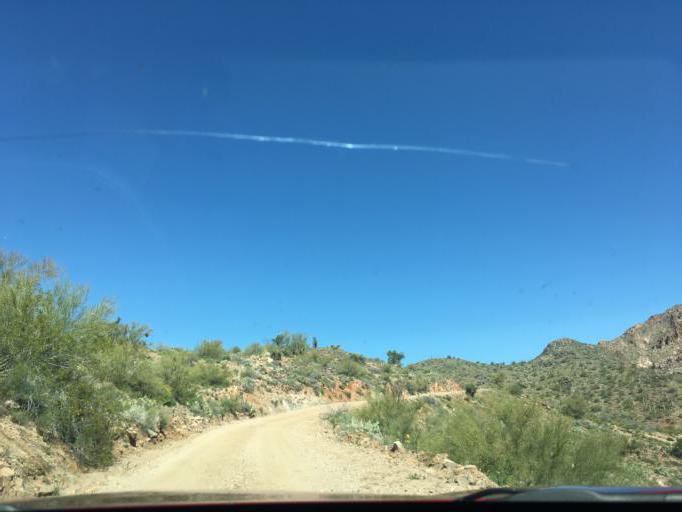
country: US
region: Arizona
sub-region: Yavapai County
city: Bagdad
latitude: 34.6084
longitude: -113.3992
